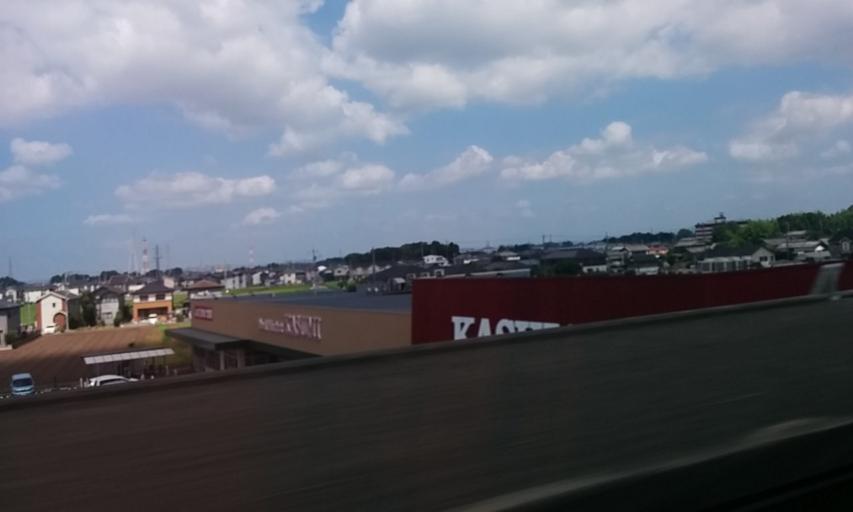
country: JP
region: Ibaraki
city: Koga
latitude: 36.1941
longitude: 139.7449
